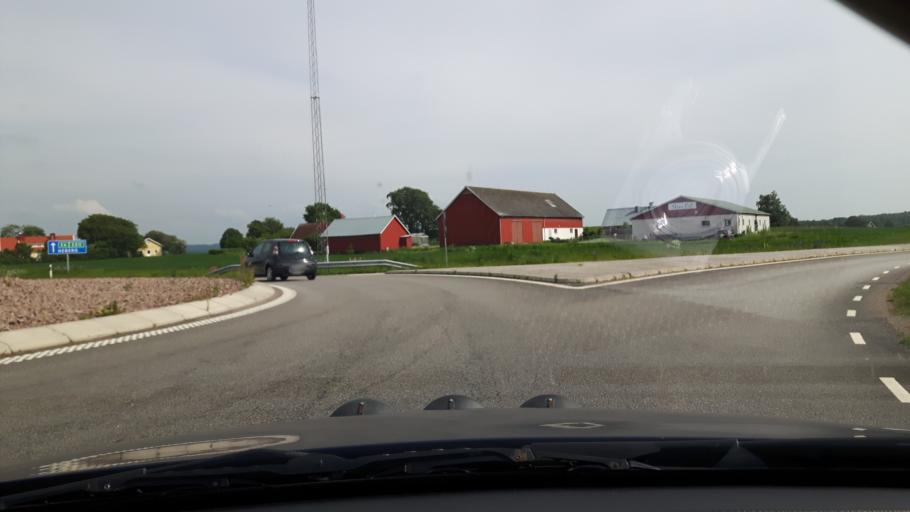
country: SE
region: Halland
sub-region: Falkenbergs Kommun
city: Falkenberg
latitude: 56.8846
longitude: 12.5691
